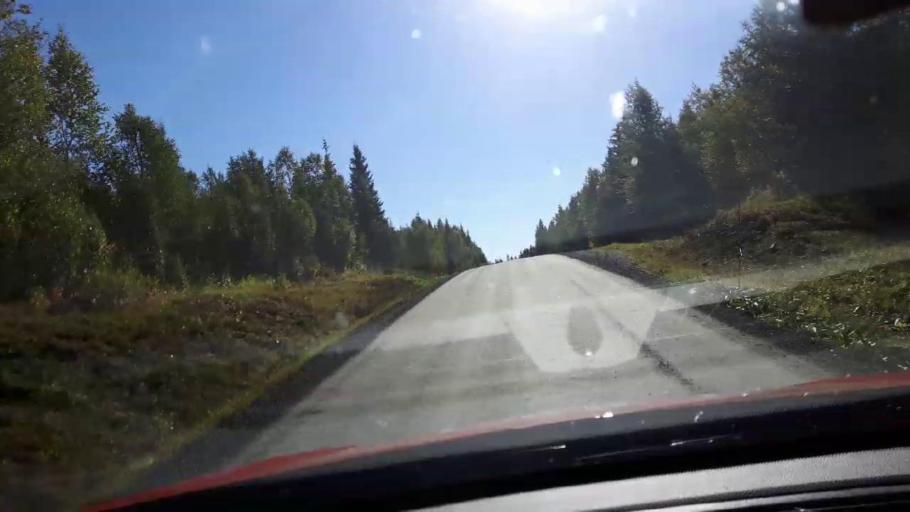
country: NO
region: Nord-Trondelag
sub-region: Lierne
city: Sandvika
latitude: 64.6012
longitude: 13.9708
